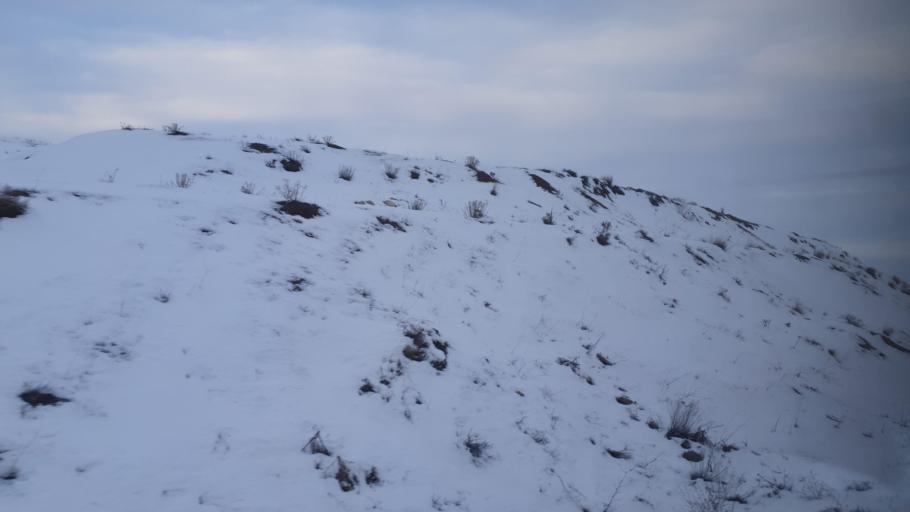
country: TR
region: Yozgat
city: Yerkoy
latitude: 39.6866
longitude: 34.4138
